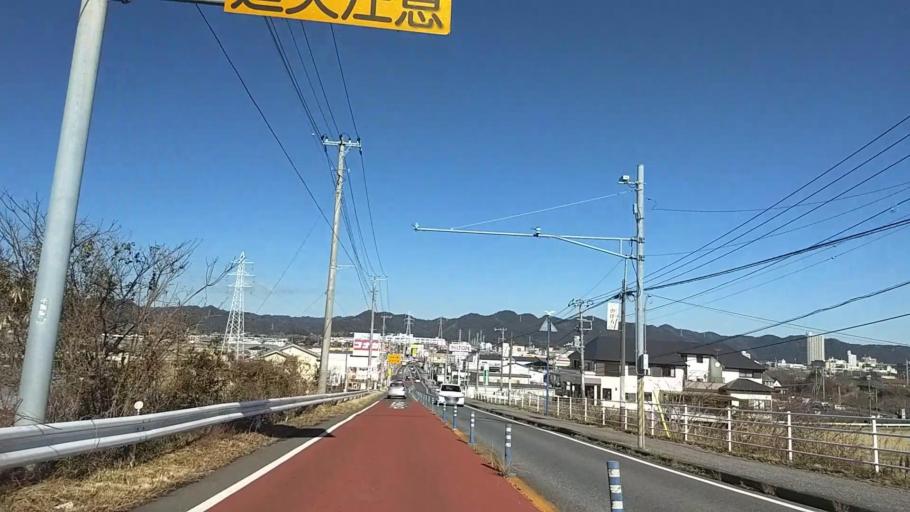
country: JP
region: Chiba
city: Kawaguchi
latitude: 35.0981
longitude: 140.0931
